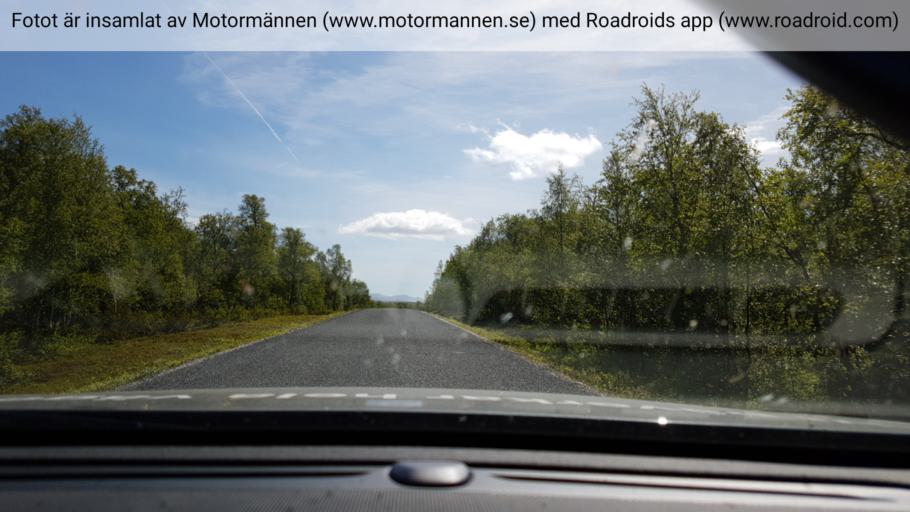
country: NO
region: Nordland
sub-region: Hattfjelldal
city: Hattfjelldal
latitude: 65.4105
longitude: 14.9353
